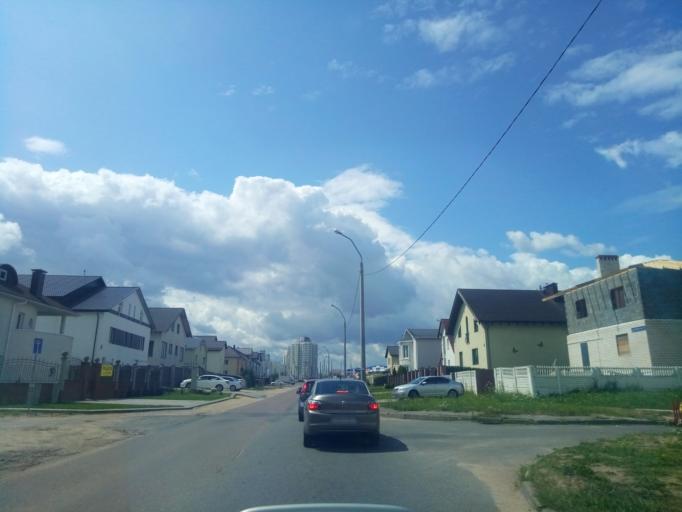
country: BY
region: Minsk
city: Zhdanovichy
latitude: 53.9378
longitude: 27.4344
